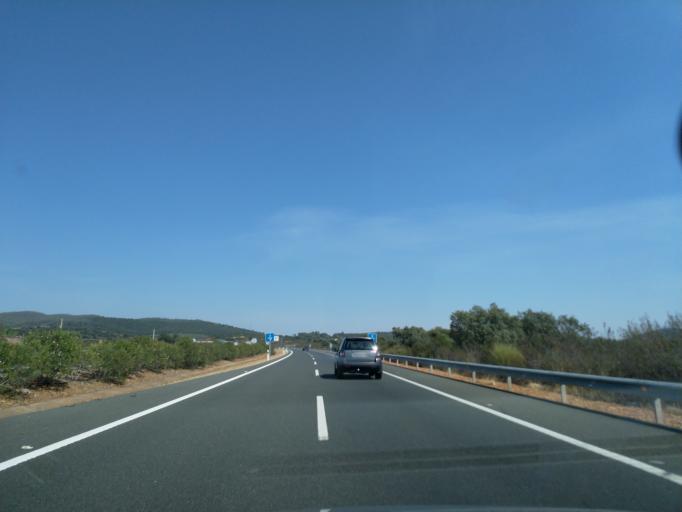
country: ES
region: Extremadura
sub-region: Provincia de Caceres
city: Alcuescar
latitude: 39.1365
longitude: -6.2742
